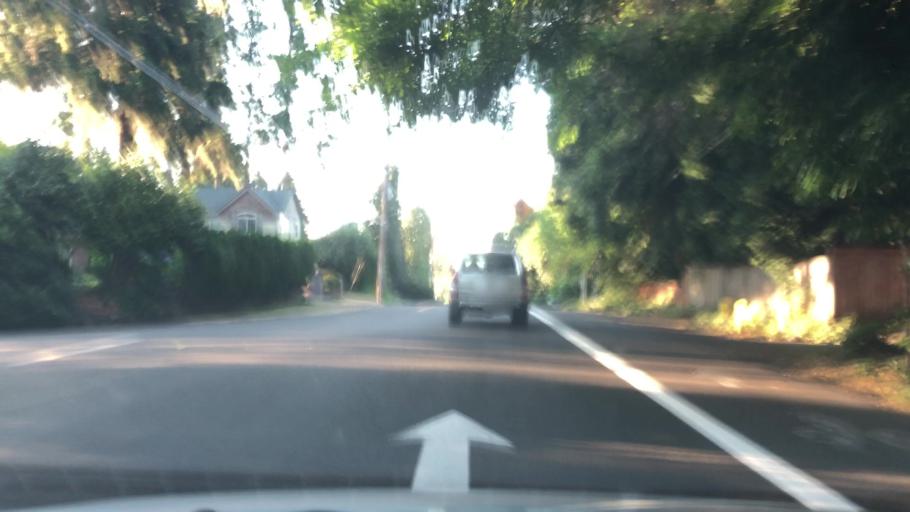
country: US
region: Oregon
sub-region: Clackamas County
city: Milwaukie
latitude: 45.4353
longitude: -122.6400
